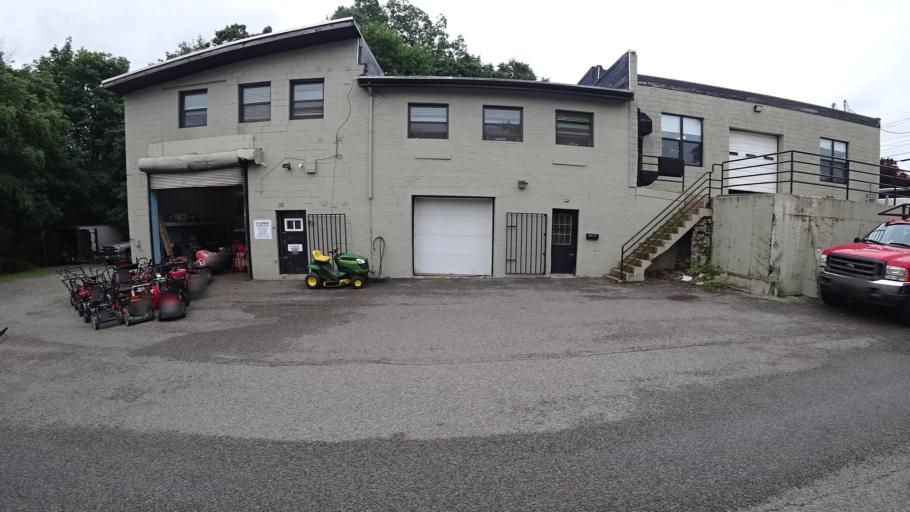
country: US
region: Massachusetts
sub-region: Norfolk County
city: Dedham
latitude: 42.2417
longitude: -71.1448
